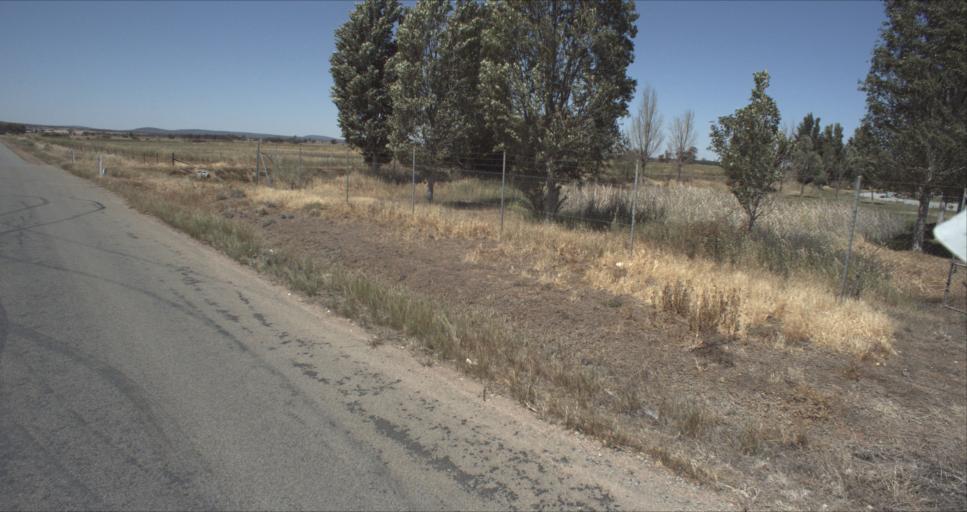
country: AU
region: New South Wales
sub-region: Leeton
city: Leeton
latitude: -34.5438
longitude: 146.4292
